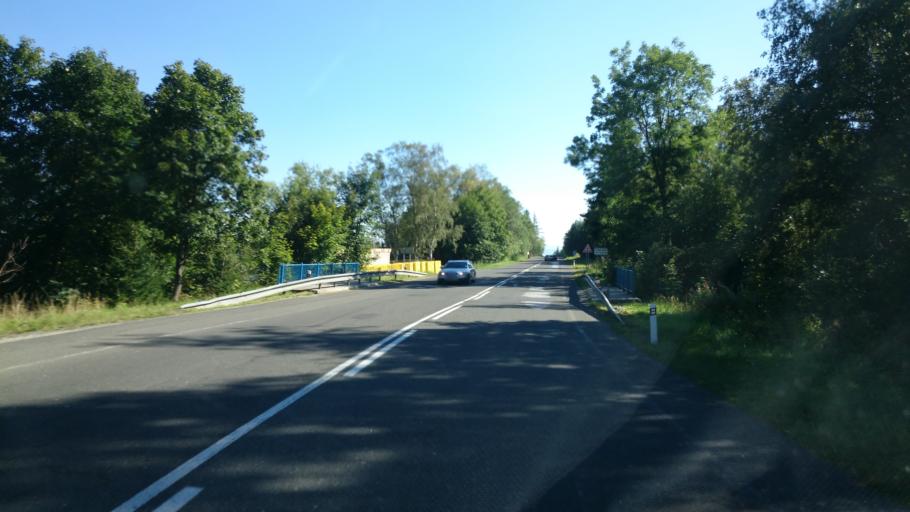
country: SK
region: Presovsky
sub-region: Okres Poprad
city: Nova Lesna
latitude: 49.1780
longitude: 20.2939
